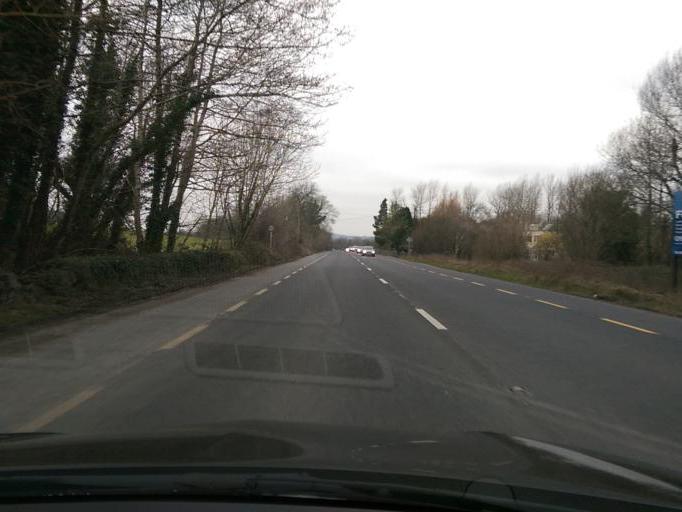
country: IE
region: Connaught
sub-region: County Galway
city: Bearna
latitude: 53.3069
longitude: -9.1197
